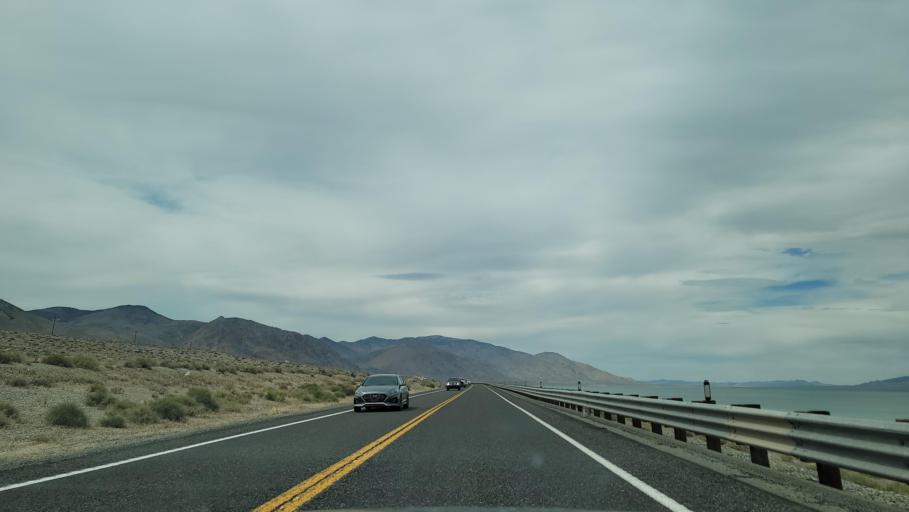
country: US
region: Nevada
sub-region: Mineral County
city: Hawthorne
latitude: 38.6032
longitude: -118.7108
